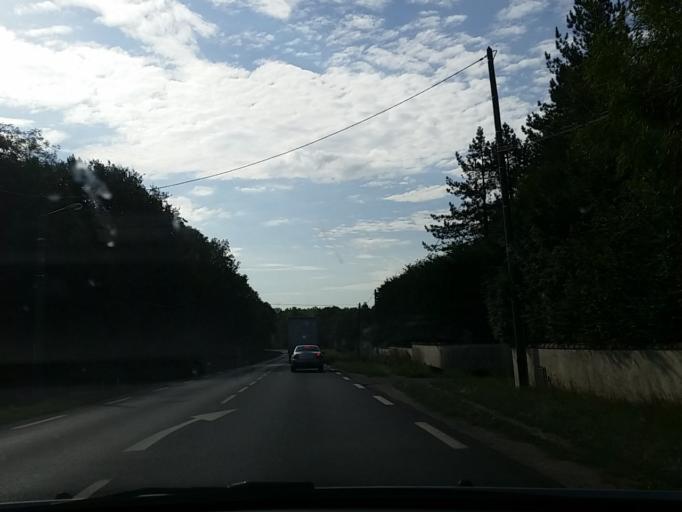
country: FR
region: Centre
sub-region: Departement du Loir-et-Cher
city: Romorantin-Lanthenay
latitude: 47.3765
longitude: 1.6883
